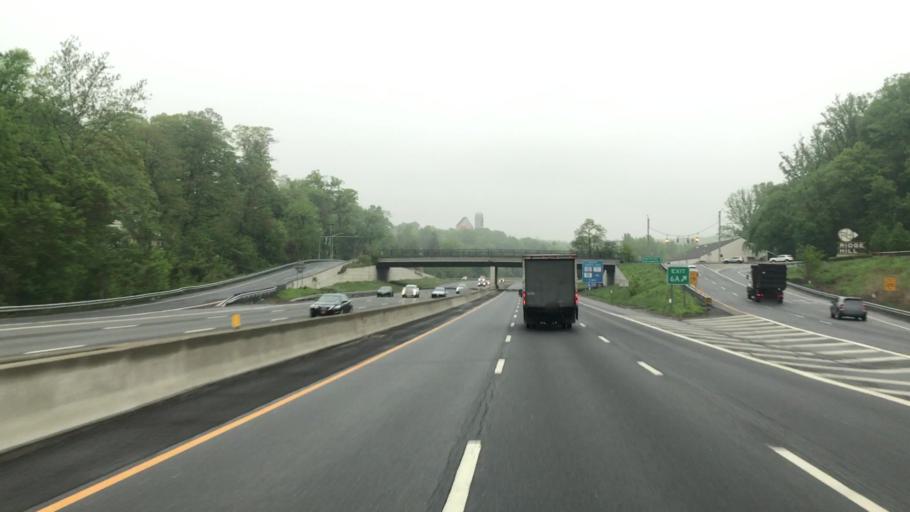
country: US
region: New York
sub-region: Westchester County
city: Hastings-on-Hudson
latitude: 40.9652
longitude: -73.8602
